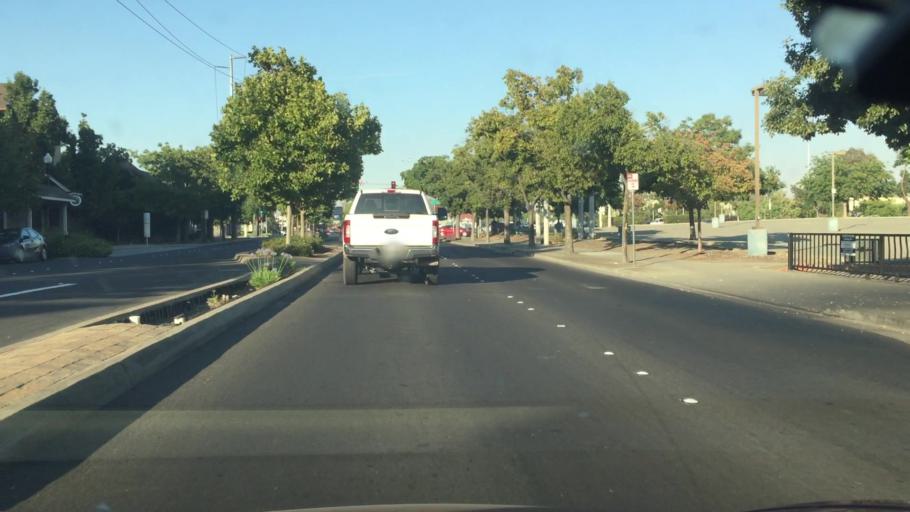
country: US
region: California
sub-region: Alameda County
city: Livermore
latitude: 37.6821
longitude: -121.7733
